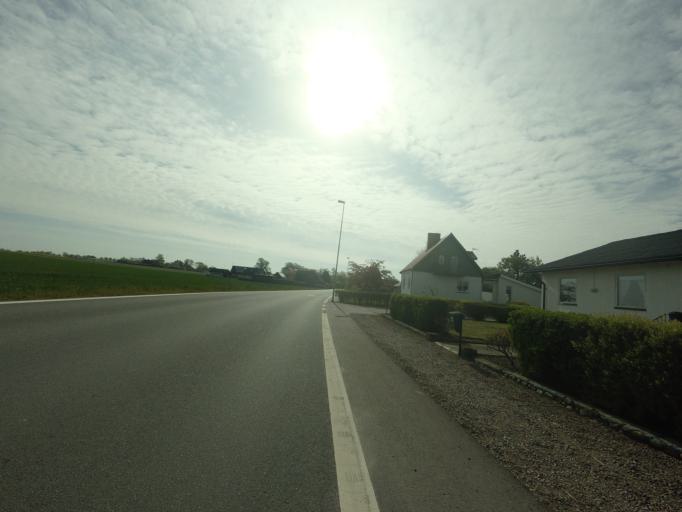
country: SE
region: Skane
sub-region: Hoganas Kommun
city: Hoganas
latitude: 56.2111
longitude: 12.5887
